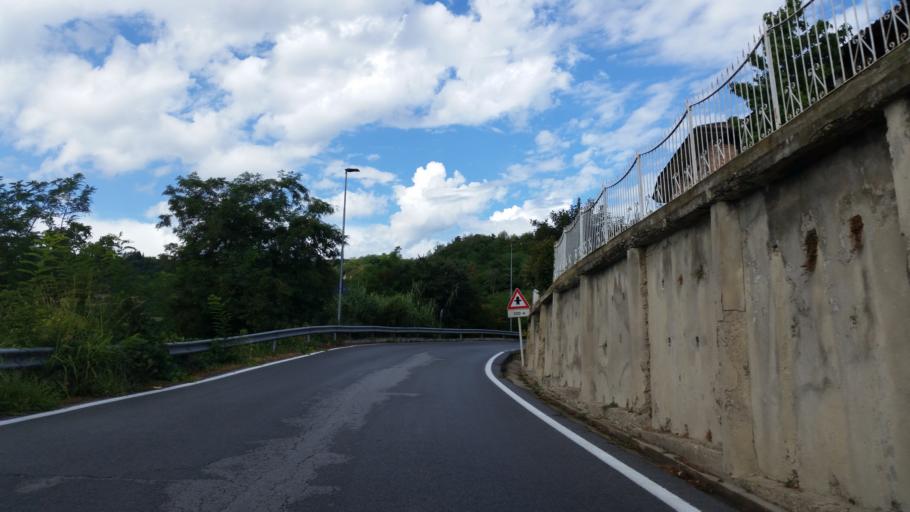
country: IT
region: Piedmont
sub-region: Provincia di Cuneo
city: Castagnito
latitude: 44.7529
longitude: 8.0494
